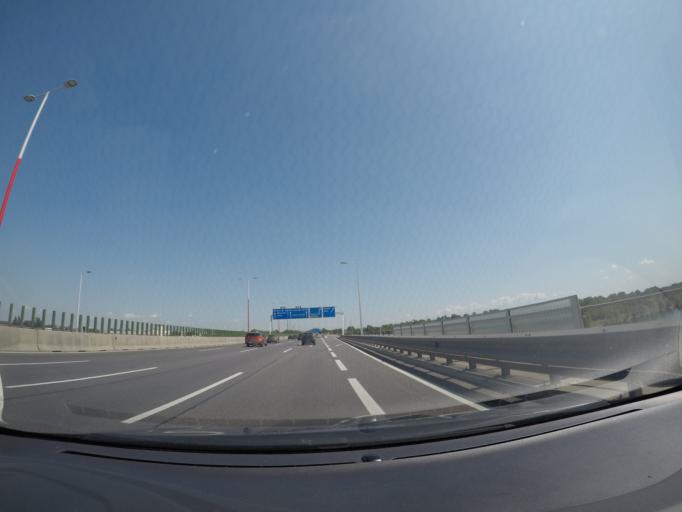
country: AT
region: Vienna
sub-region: Wien Stadt
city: Vienna
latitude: 48.2071
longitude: 16.4420
